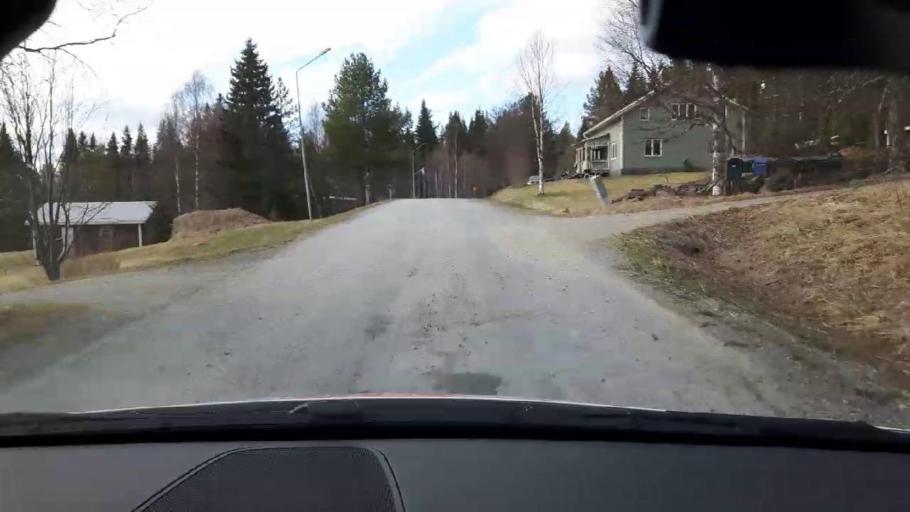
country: SE
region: Jaemtland
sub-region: Bergs Kommun
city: Hoverberg
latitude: 62.6670
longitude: 14.7476
